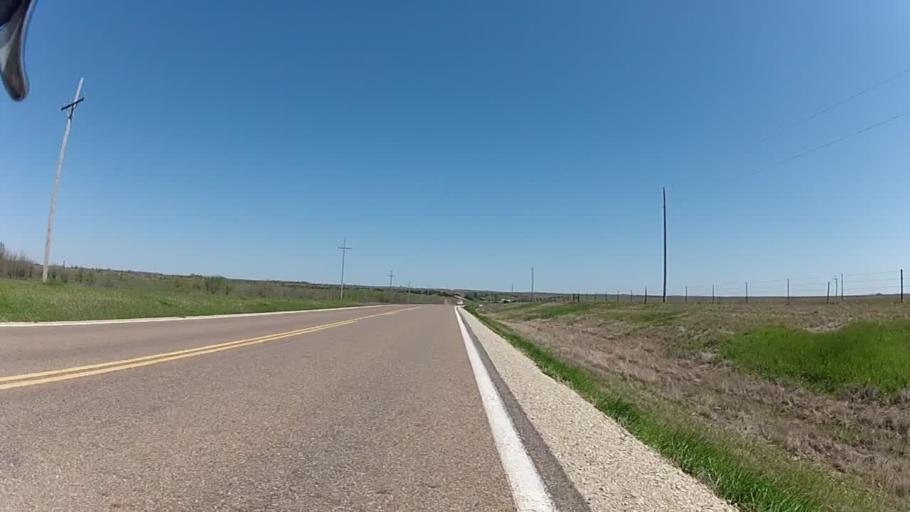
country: US
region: Kansas
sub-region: Wabaunsee County
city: Alma
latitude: 38.9159
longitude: -96.5203
